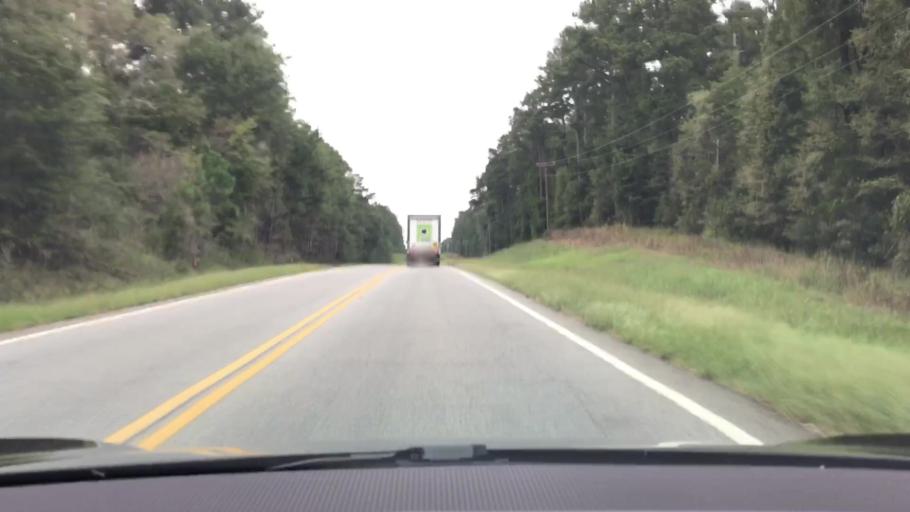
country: US
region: Georgia
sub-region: Greene County
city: Greensboro
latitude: 33.6557
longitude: -83.2382
